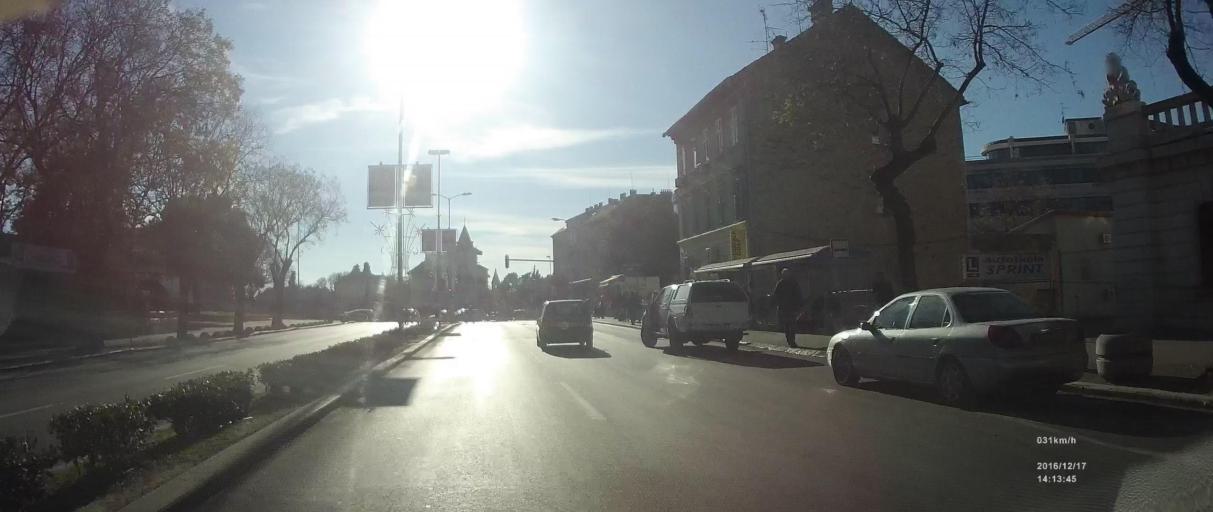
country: HR
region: Splitsko-Dalmatinska
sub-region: Grad Split
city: Split
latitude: 43.5131
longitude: 16.4427
